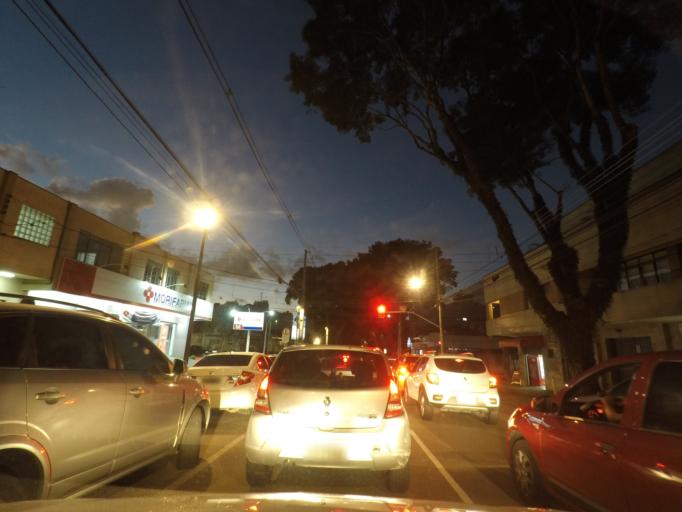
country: BR
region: Parana
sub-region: Curitiba
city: Curitiba
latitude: -25.4507
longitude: -49.2775
